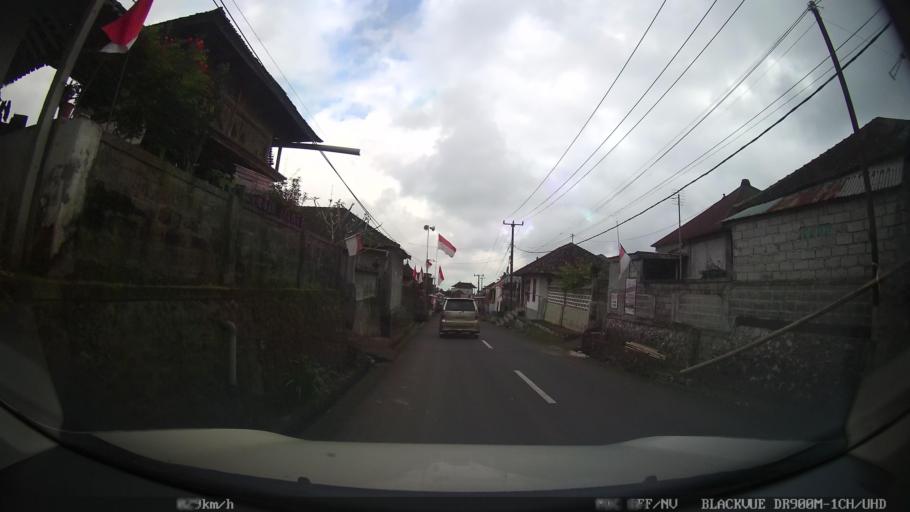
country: ID
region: Bali
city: Peneng
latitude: -8.3532
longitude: 115.1844
